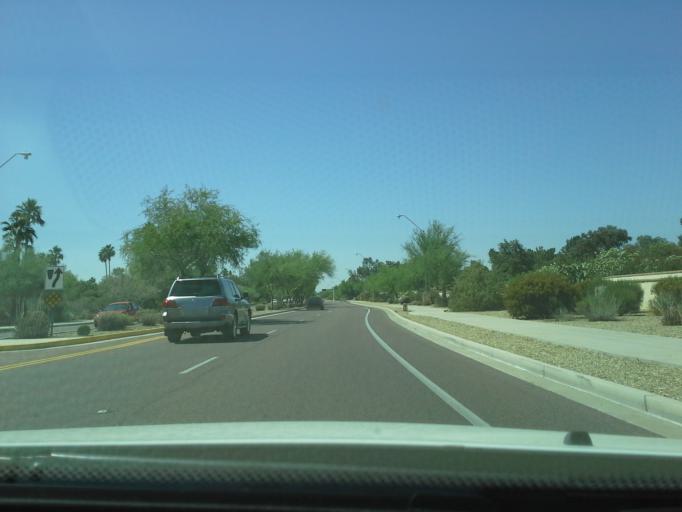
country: US
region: Arizona
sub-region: Maricopa County
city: Paradise Valley
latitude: 33.6030
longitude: -111.9086
